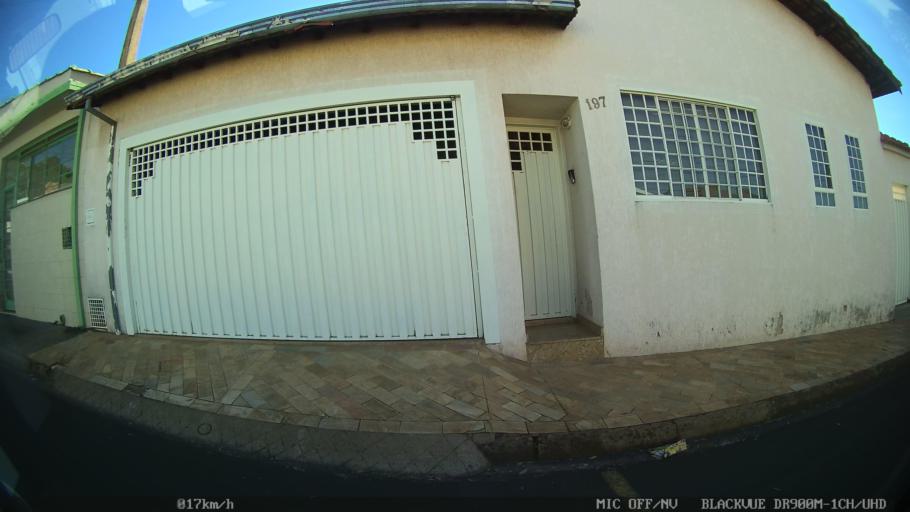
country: BR
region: Sao Paulo
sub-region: Franca
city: Franca
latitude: -20.5292
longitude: -47.4112
